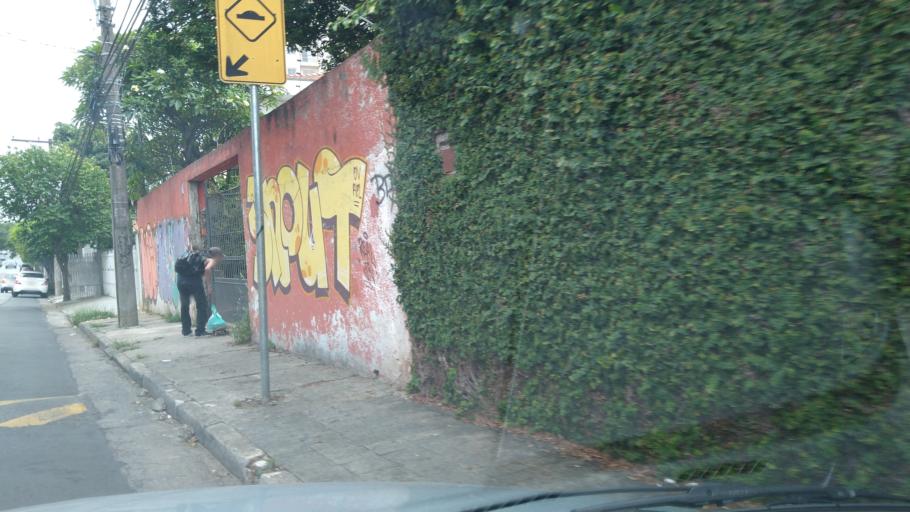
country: BR
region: Sao Paulo
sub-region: Guarulhos
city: Guarulhos
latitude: -23.4873
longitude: -46.5907
